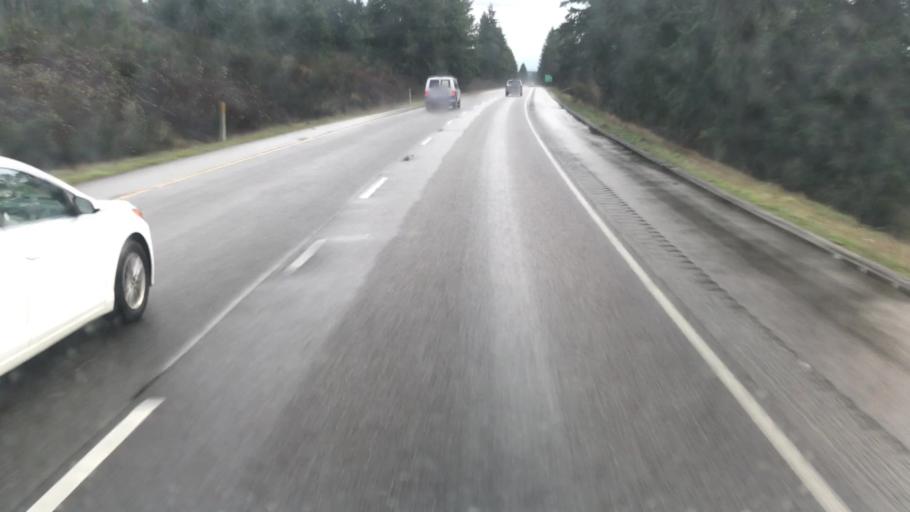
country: US
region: Washington
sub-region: Kitsap County
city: Burley
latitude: 47.4527
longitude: -122.6218
